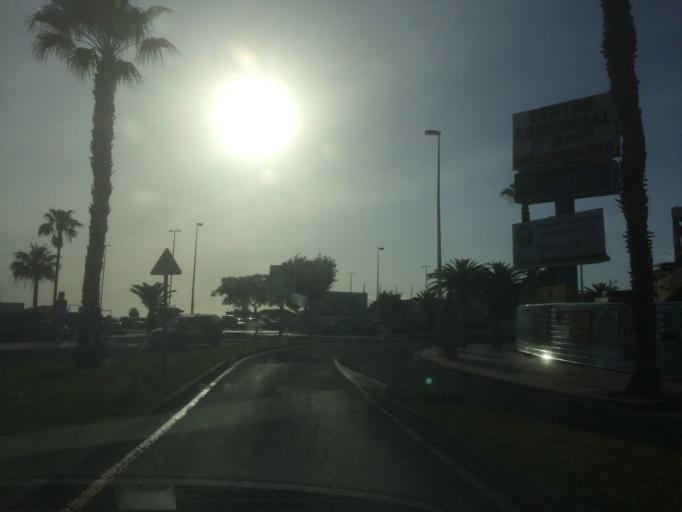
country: ES
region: Canary Islands
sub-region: Provincia de Santa Cruz de Tenerife
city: Playa de las Americas
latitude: 28.0915
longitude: -16.7351
